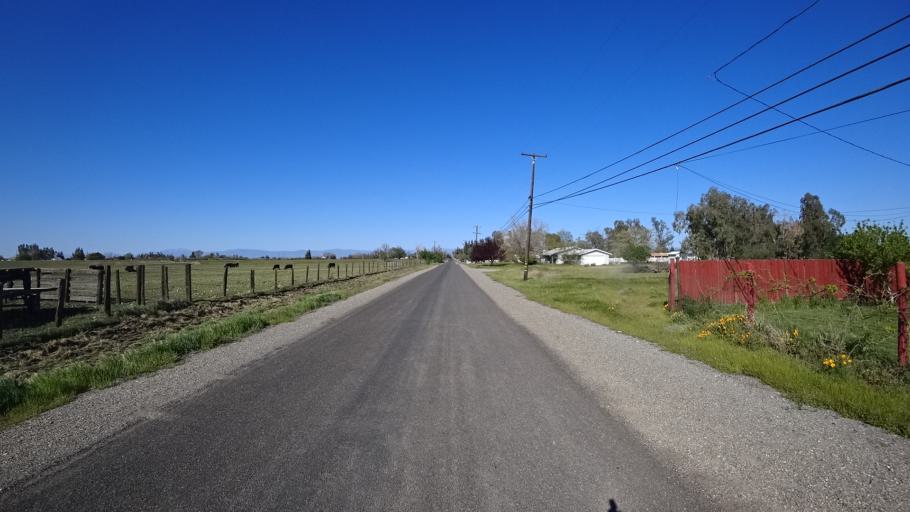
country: US
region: California
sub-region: Glenn County
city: Orland
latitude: 39.7439
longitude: -122.2094
